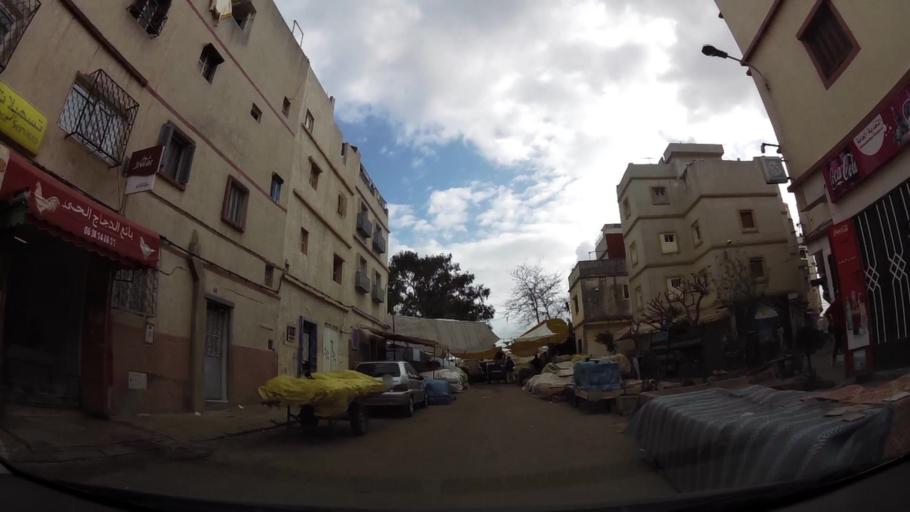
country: MA
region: Tanger-Tetouan
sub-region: Tanger-Assilah
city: Tangier
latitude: 35.7645
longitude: -5.8244
